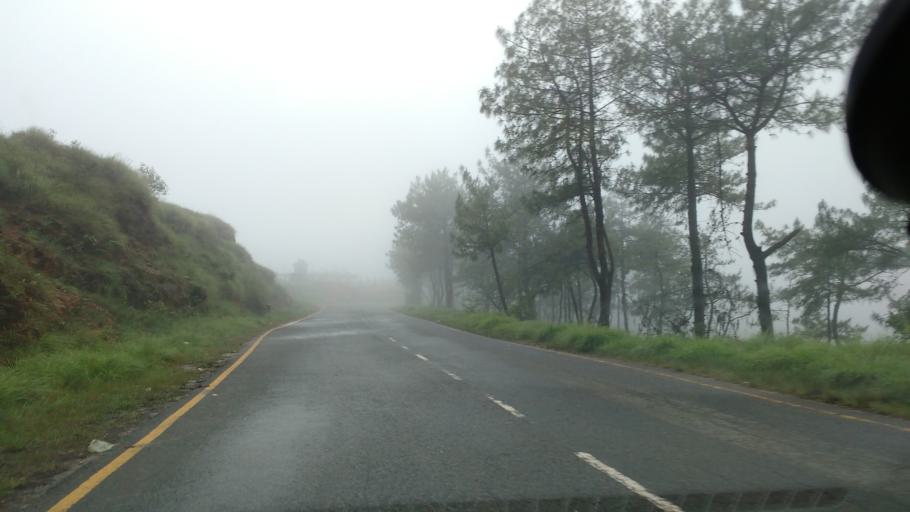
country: IN
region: Meghalaya
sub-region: East Khasi Hills
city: Cherrapunji
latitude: 25.2902
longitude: 91.7137
